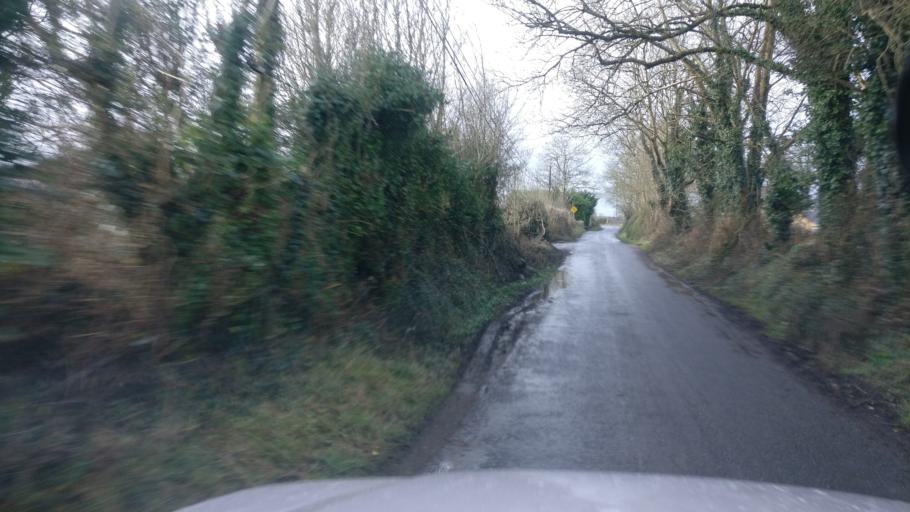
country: IE
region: Connaught
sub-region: County Galway
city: Athenry
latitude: 53.2775
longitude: -8.7634
